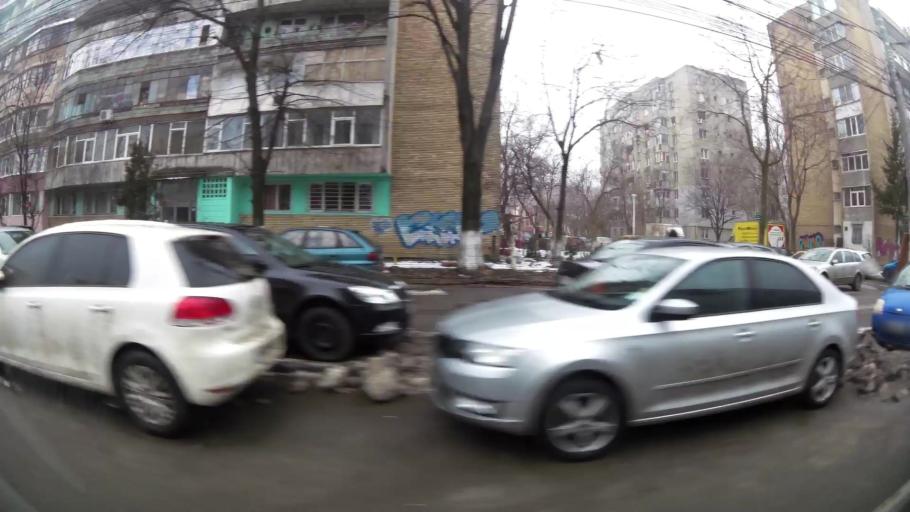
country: RO
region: Ilfov
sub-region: Comuna Chiajna
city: Rosu
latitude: 44.4597
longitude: 26.0486
